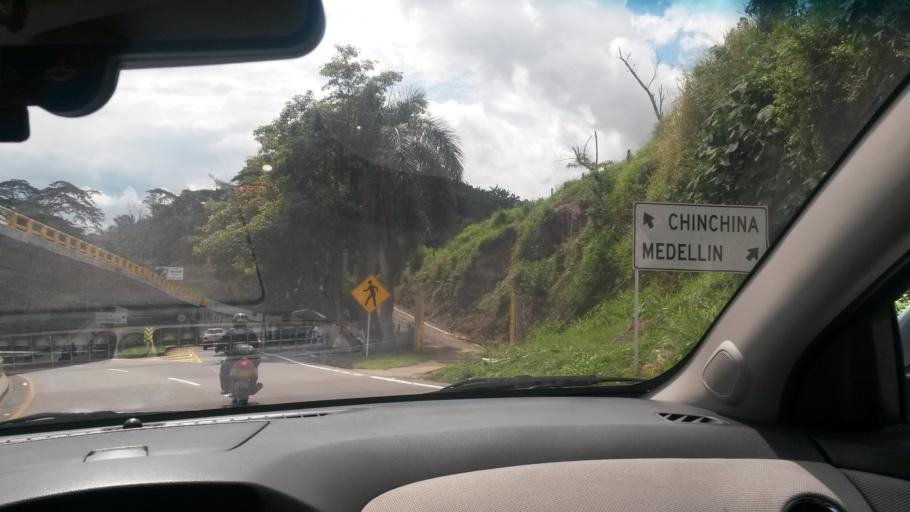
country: CO
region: Caldas
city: Palestina
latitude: 5.0425
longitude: -75.5793
